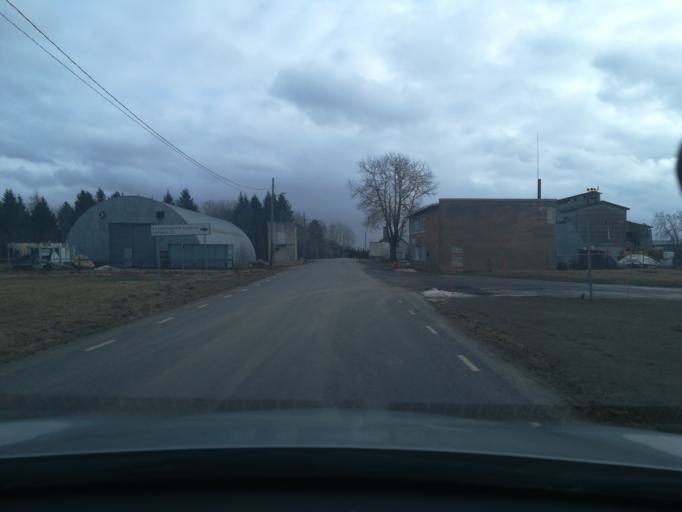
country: EE
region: Harju
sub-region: Saue linn
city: Saue
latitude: 59.3428
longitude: 24.5527
